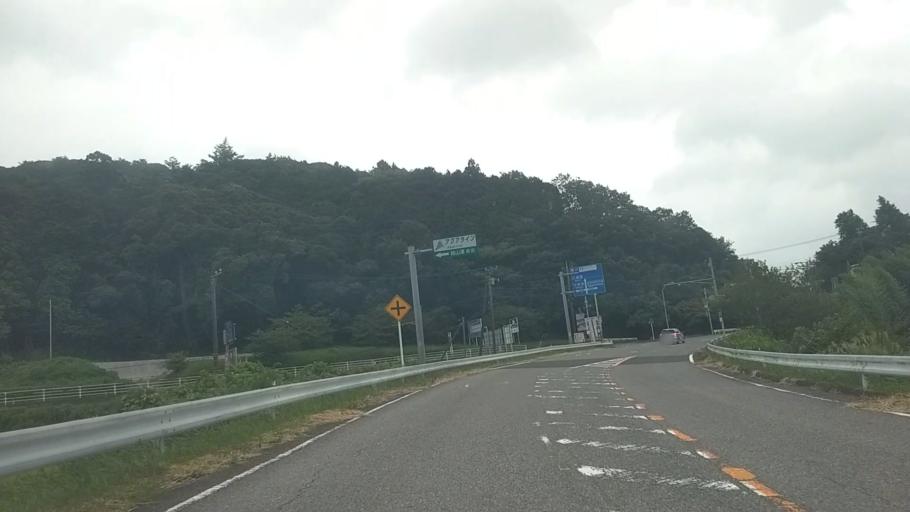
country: JP
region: Chiba
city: Kimitsu
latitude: 35.2489
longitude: 140.0007
